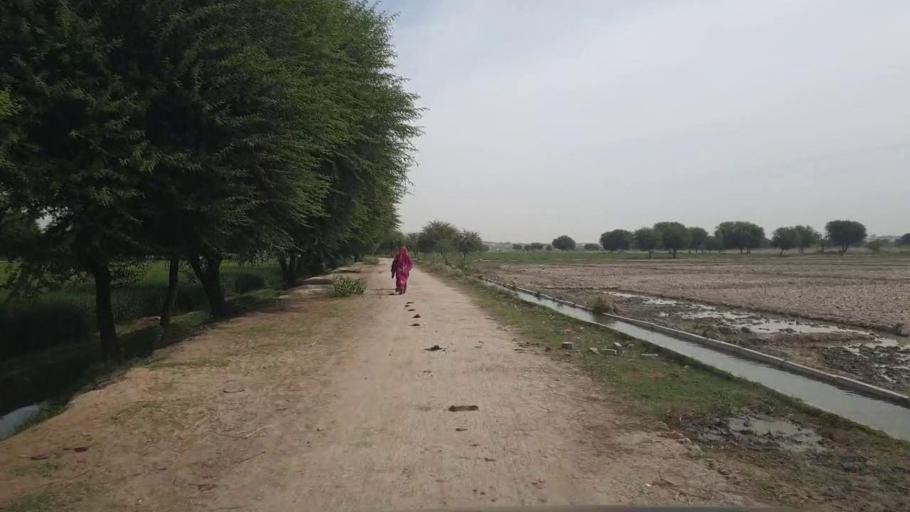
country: PK
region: Sindh
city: Umarkot
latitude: 25.2323
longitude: 69.6989
